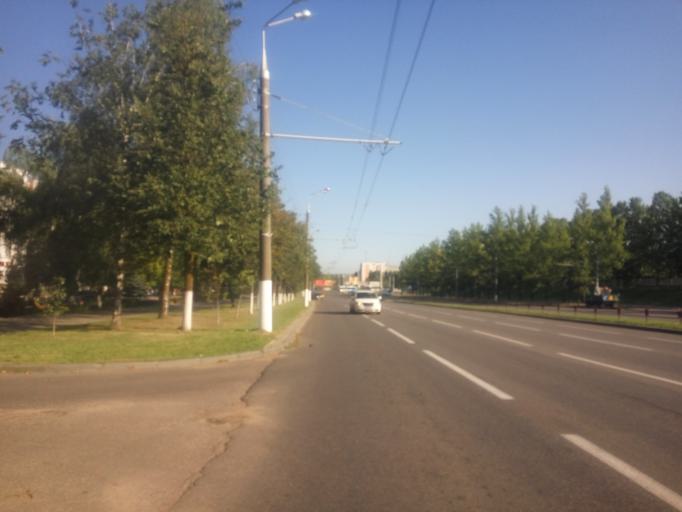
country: BY
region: Vitebsk
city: Vitebsk
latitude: 55.1932
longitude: 30.2495
